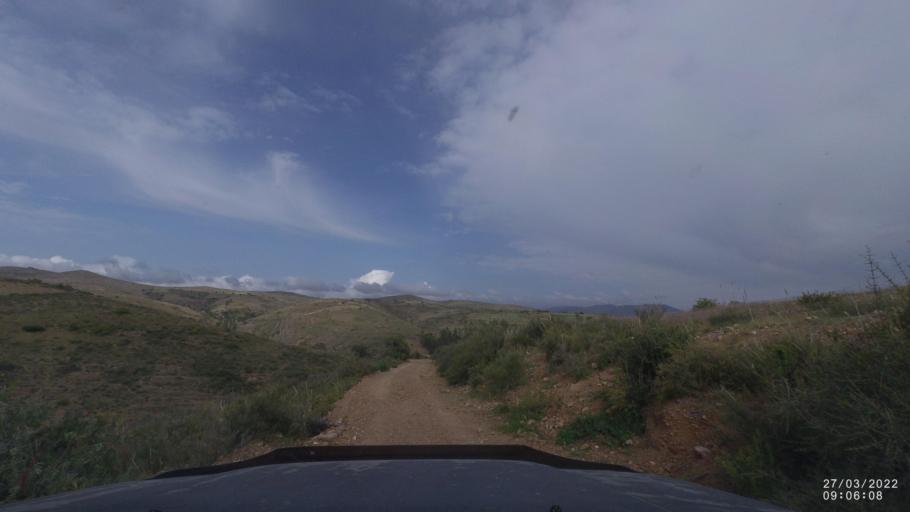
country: BO
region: Cochabamba
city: Cliza
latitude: -17.7316
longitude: -65.8705
